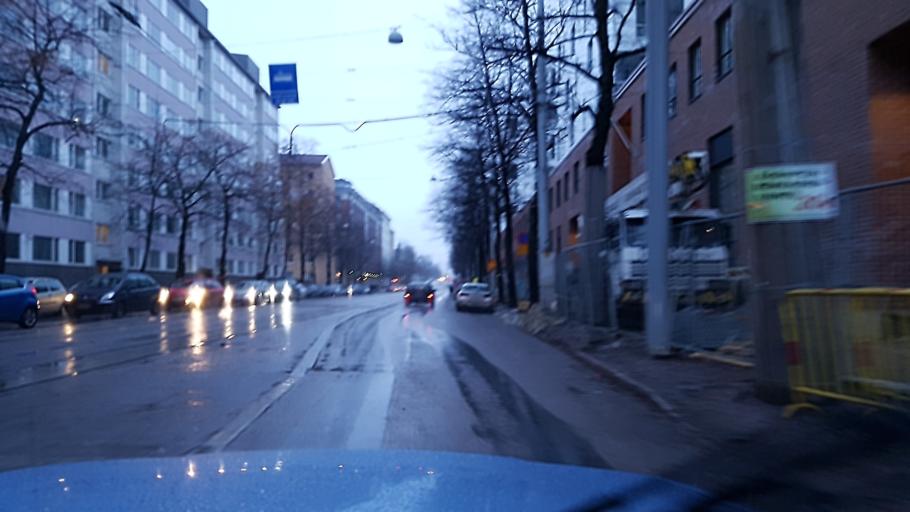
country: FI
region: Uusimaa
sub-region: Helsinki
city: Helsinki
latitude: 60.1911
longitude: 24.9483
